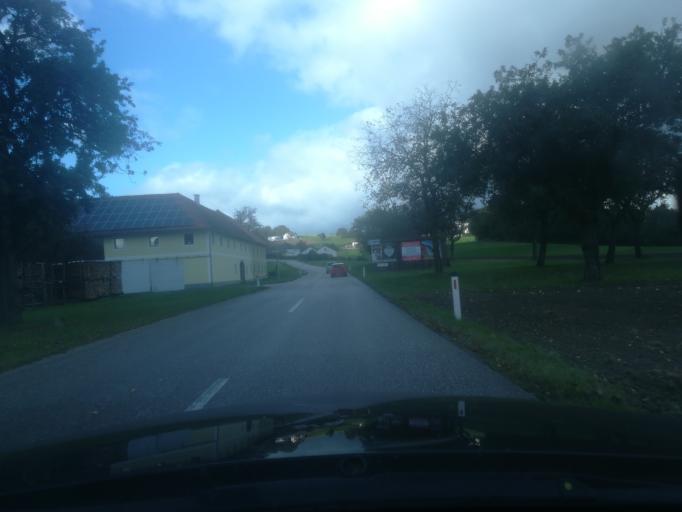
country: AT
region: Upper Austria
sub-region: Linz Stadt
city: Linz
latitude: 48.3502
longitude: 14.2647
